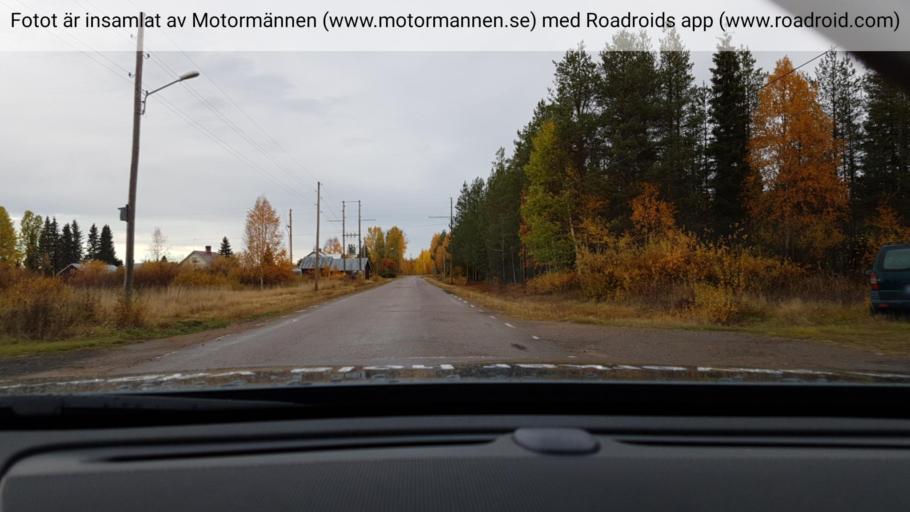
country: SE
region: Norrbotten
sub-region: Pajala Kommun
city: Pajala
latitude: 67.1713
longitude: 22.6509
